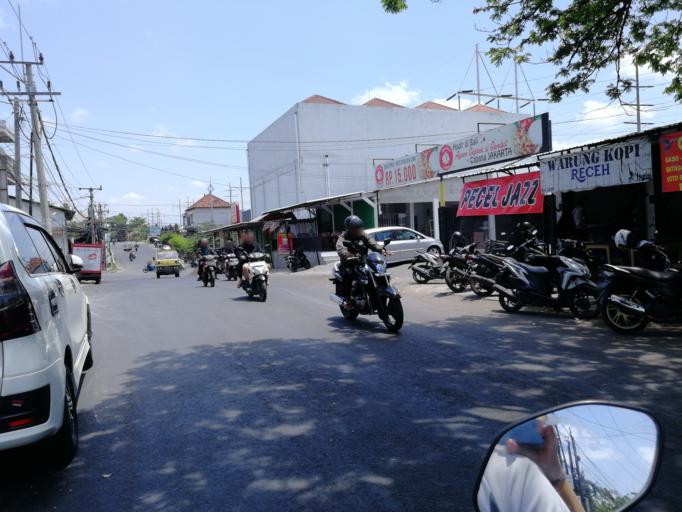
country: ID
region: Bali
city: Banjar Kertasari
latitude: -8.6378
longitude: 115.1785
